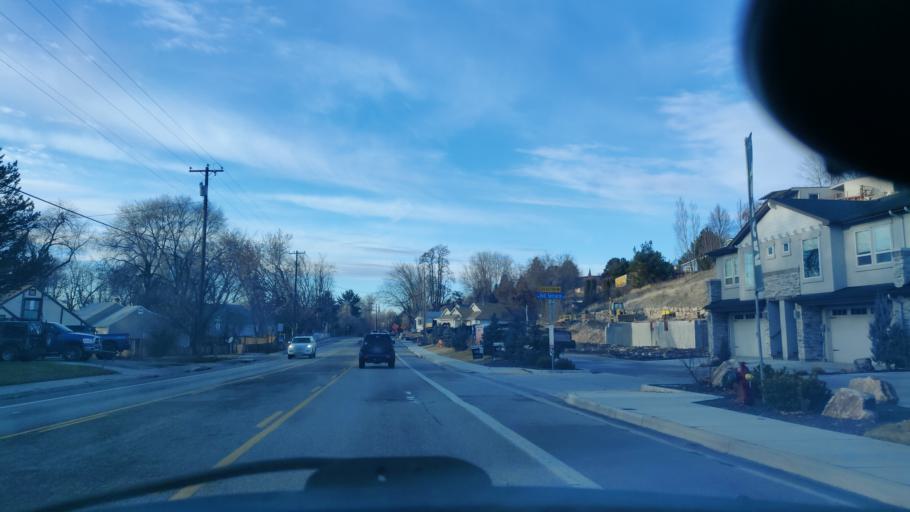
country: US
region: Idaho
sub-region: Ada County
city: Garden City
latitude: 43.6450
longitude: -116.2169
